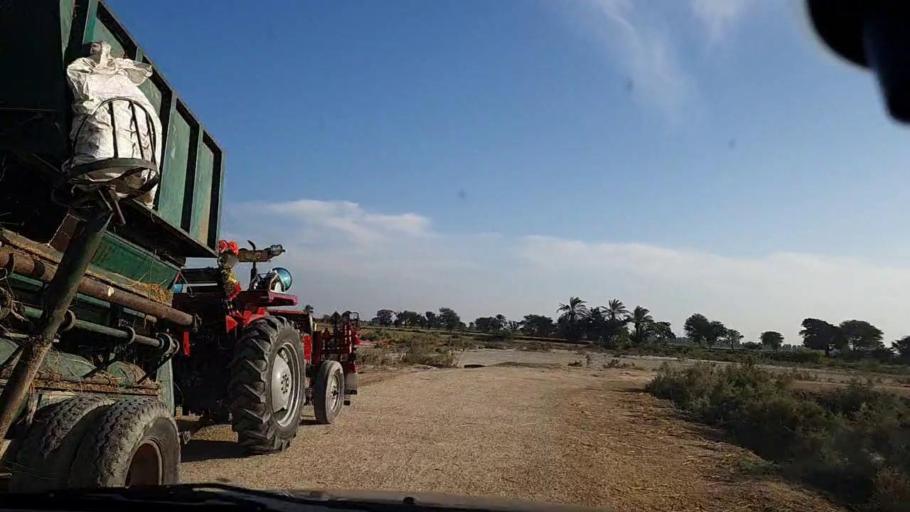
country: PK
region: Sindh
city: Mirpur Batoro
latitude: 24.6538
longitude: 68.3093
